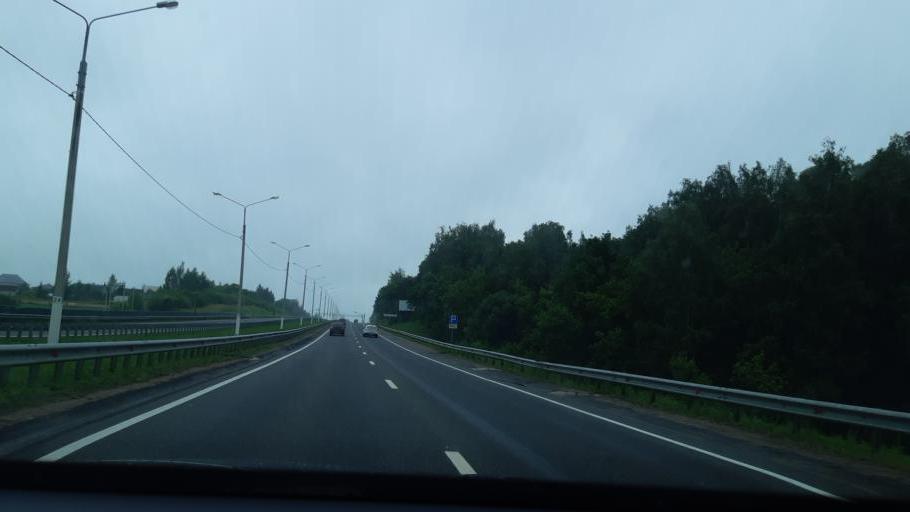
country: RU
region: Smolensk
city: Talashkino
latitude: 54.6771
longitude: 32.1440
